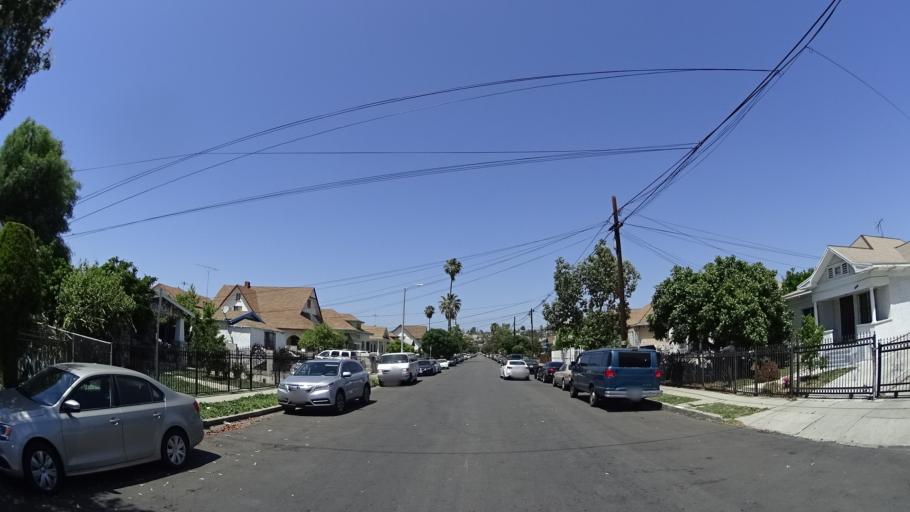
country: US
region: California
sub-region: Los Angeles County
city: Boyle Heights
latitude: 34.0686
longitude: -118.2090
